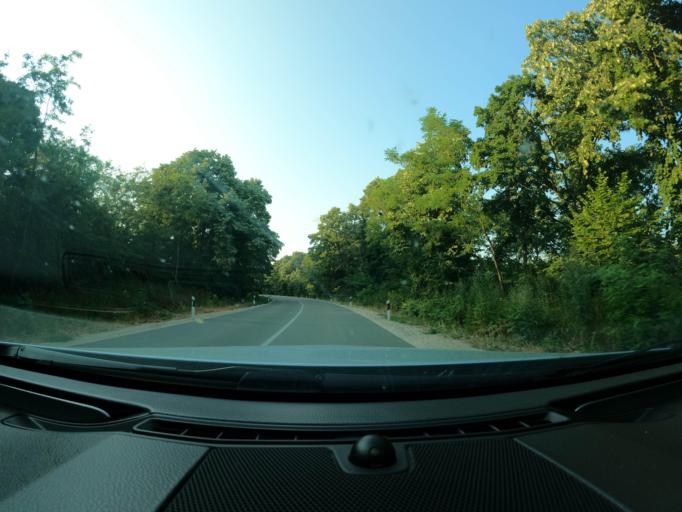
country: RS
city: Vrdnik
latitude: 45.1280
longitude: 19.7266
